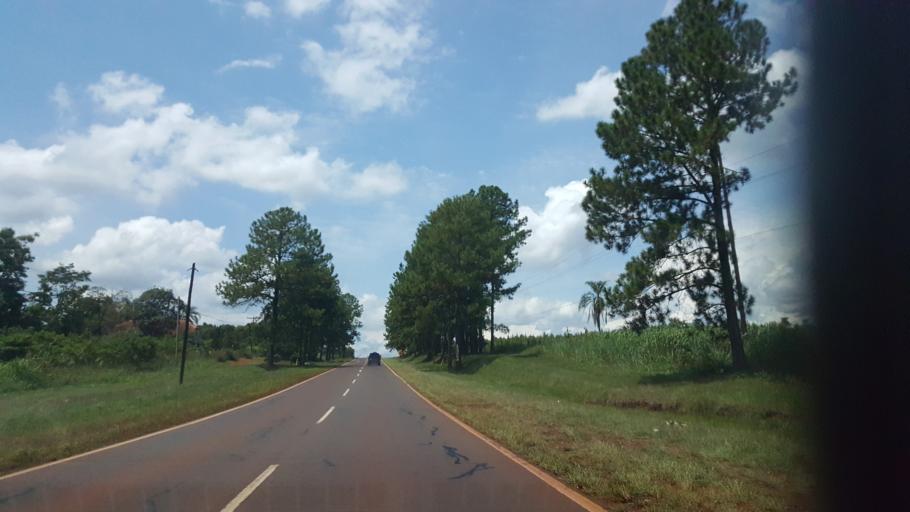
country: AR
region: Misiones
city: Puerto Rico
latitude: -26.8206
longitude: -54.9953
